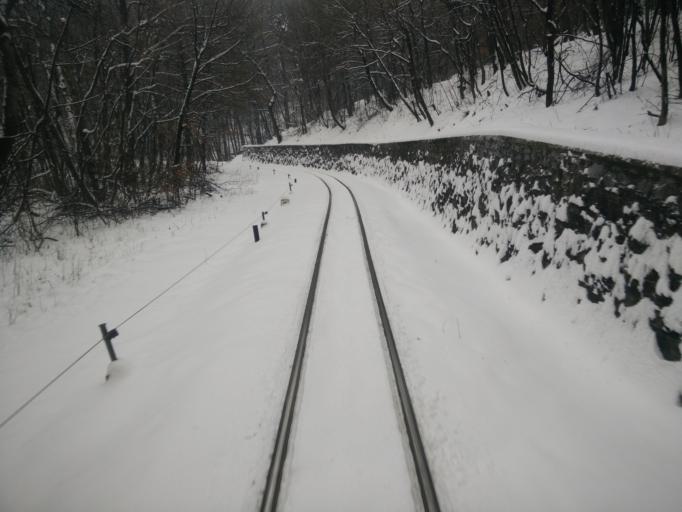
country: HU
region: Pest
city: Budakeszi
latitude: 47.5172
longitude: 18.9537
